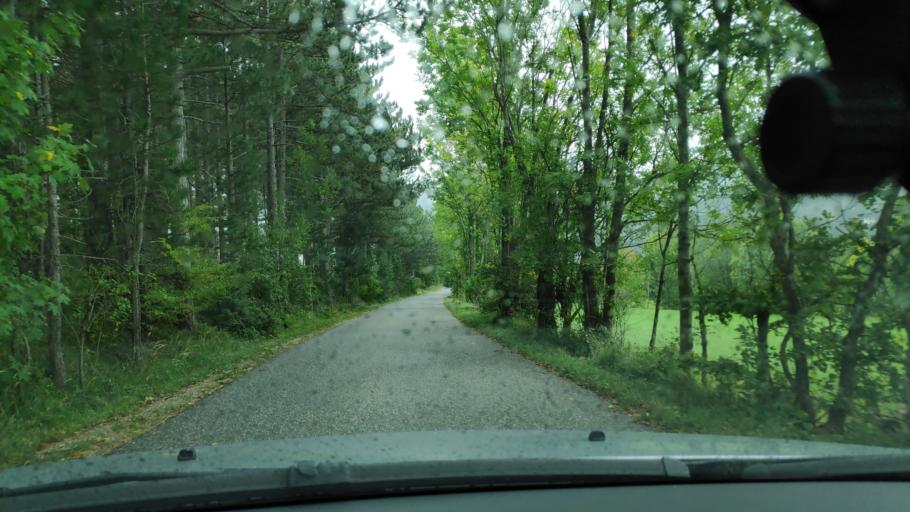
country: AT
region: Lower Austria
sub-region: Politischer Bezirk Neunkirchen
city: Grunbach am Schneeberg
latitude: 47.8019
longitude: 15.9926
